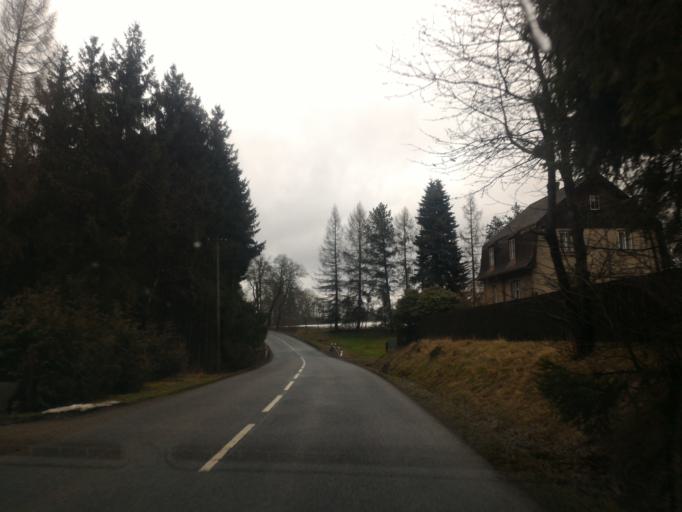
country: CZ
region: Ustecky
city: Stare Krecany
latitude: 50.9306
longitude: 14.4839
